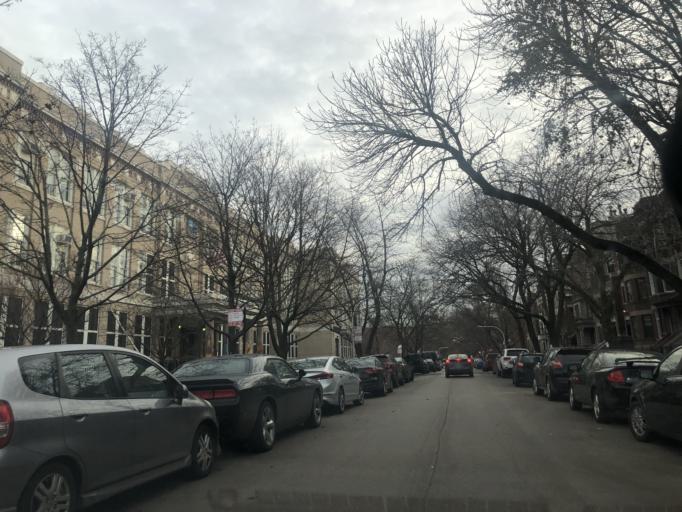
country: US
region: Illinois
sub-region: Cook County
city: Lincolnwood
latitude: 41.9490
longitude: -87.6520
